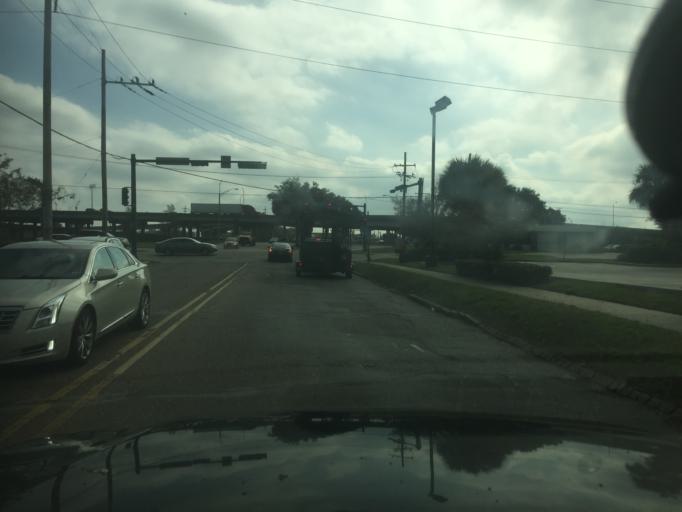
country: US
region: Louisiana
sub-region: Saint Bernard Parish
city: Arabi
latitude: 30.0045
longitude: -90.0360
